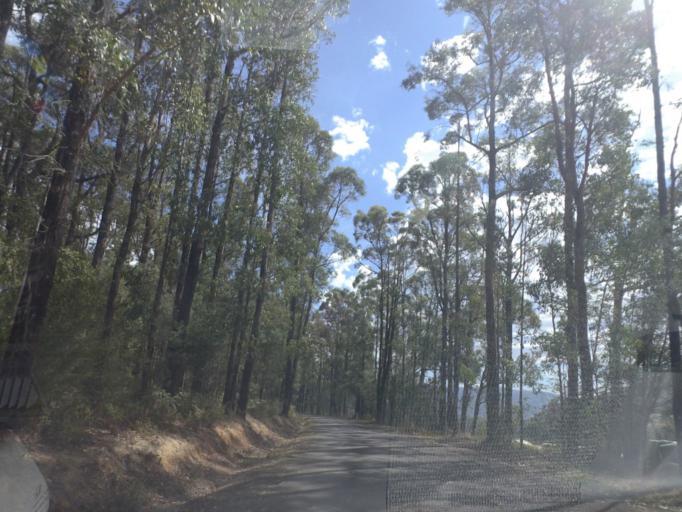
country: AU
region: Victoria
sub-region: Murrindindi
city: Alexandra
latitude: -37.4481
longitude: 145.7487
